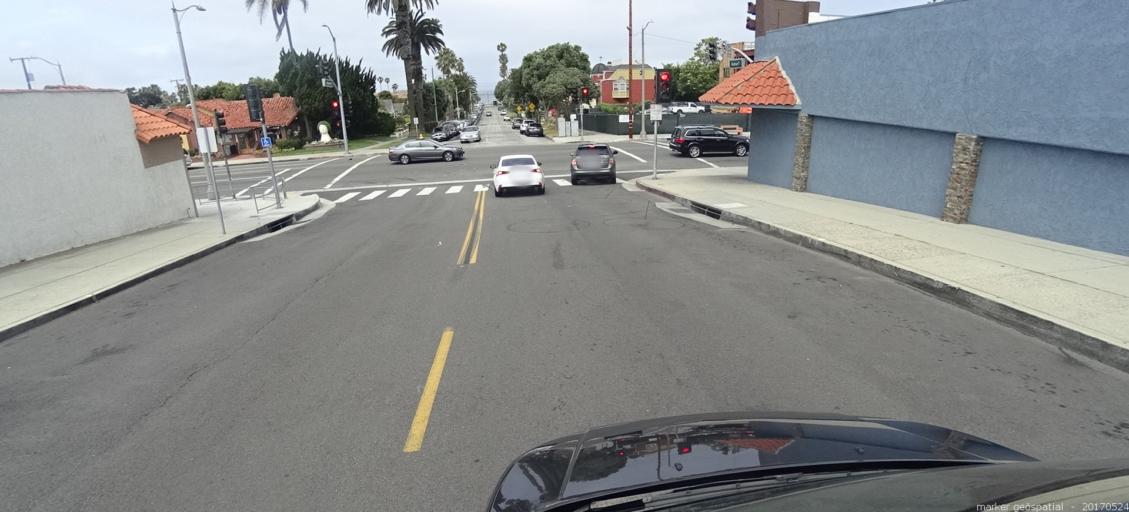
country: US
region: California
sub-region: Los Angeles County
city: Palos Verdes Estates
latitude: 33.8226
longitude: -118.3850
